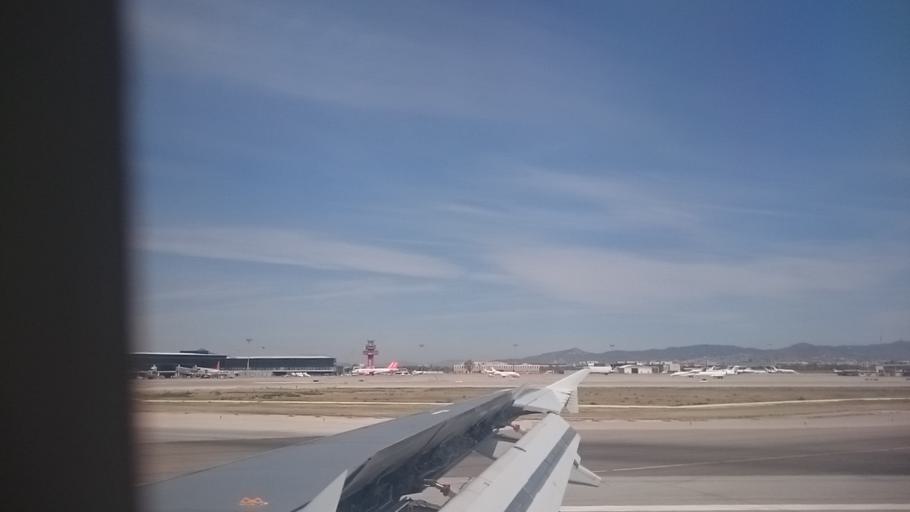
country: ES
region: Catalonia
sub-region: Provincia de Barcelona
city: El Prat de Llobregat
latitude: 41.3006
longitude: 2.0875
